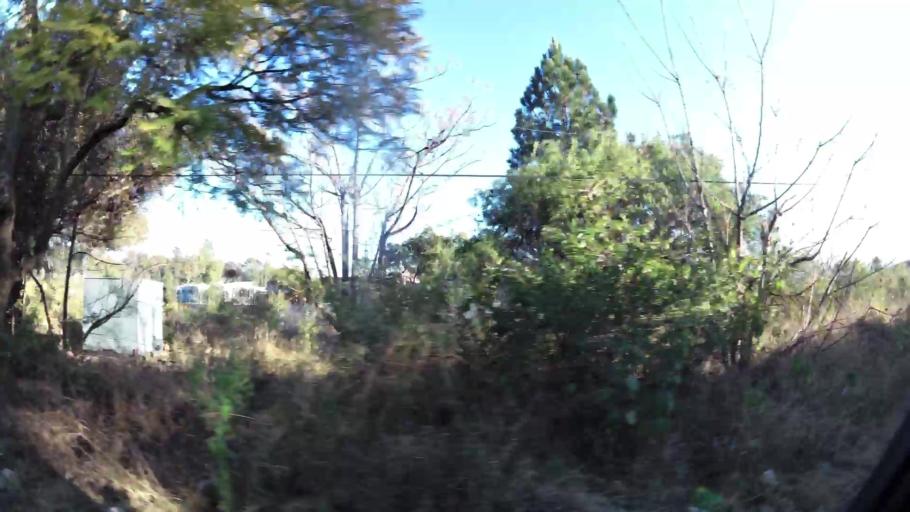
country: ZA
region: Gauteng
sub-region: City of Johannesburg Metropolitan Municipality
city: Midrand
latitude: -26.0274
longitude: 28.0404
